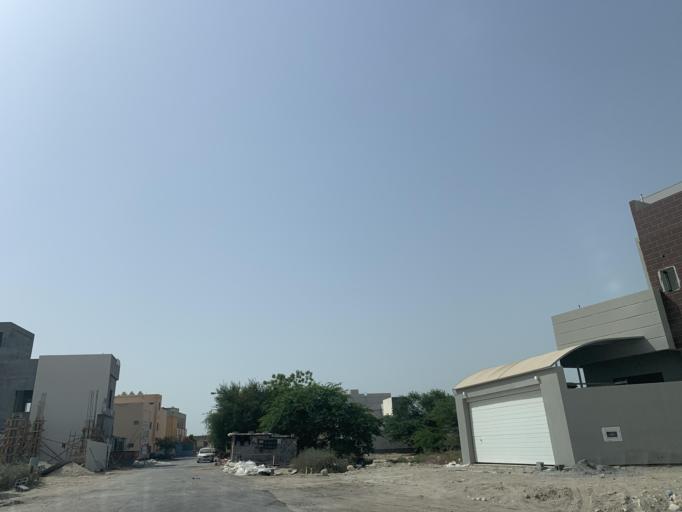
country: BH
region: Manama
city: Jidd Hafs
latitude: 26.2101
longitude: 50.5153
